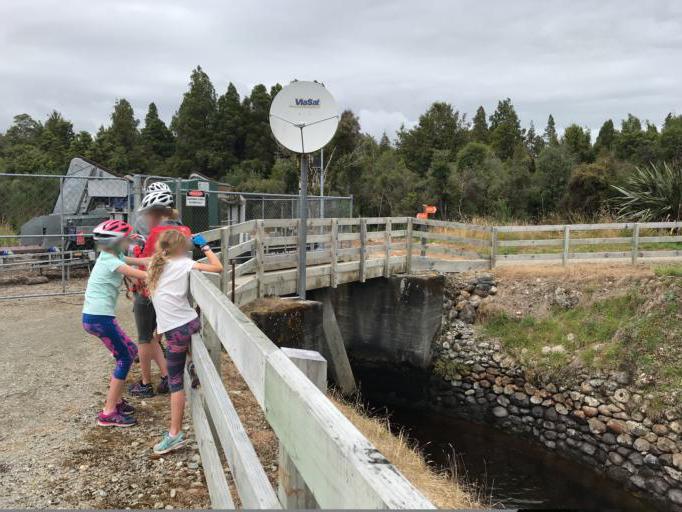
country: NZ
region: West Coast
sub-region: Westland District
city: Hokitika
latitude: -42.7681
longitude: 171.0861
